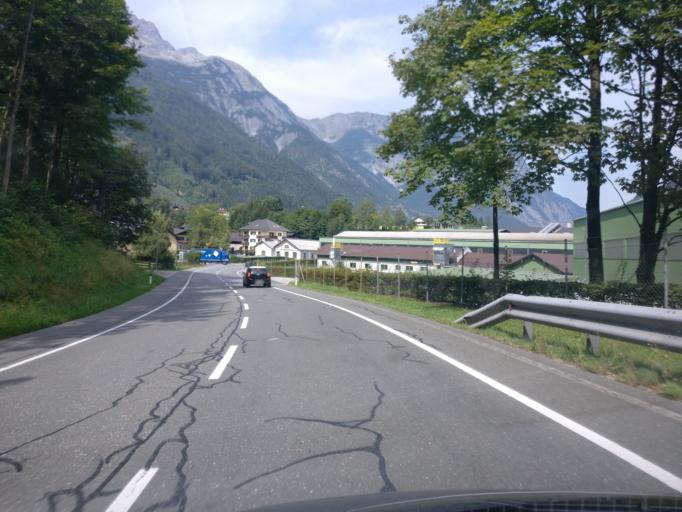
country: AT
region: Salzburg
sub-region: Politischer Bezirk Sankt Johann im Pongau
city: Werfen
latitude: 47.4912
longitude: 13.1769
